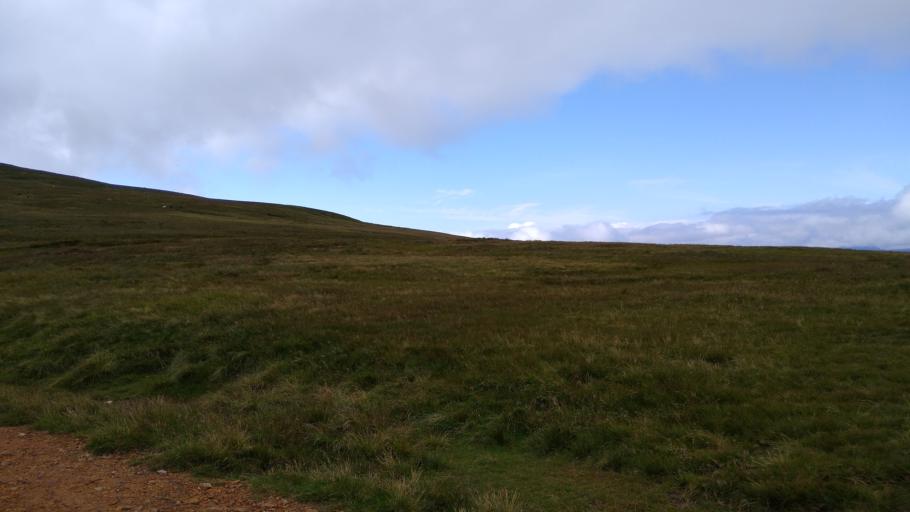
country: GB
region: England
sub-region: Cumbria
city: Keswick
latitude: 54.5546
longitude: -3.0184
